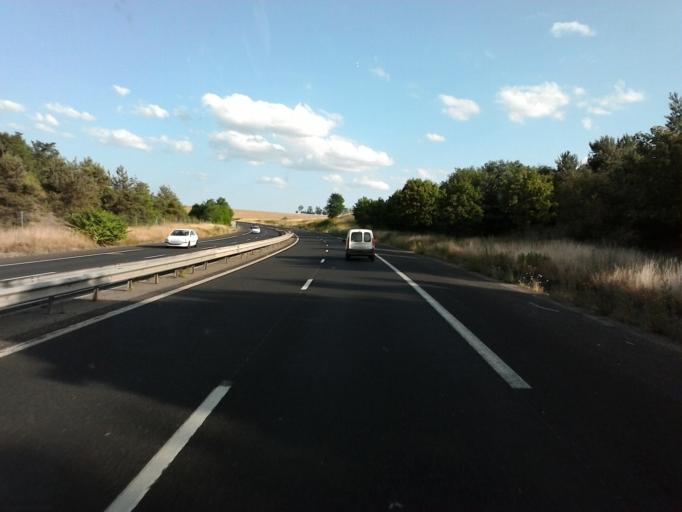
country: FR
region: Lorraine
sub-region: Departement de Meurthe-et-Moselle
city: Flavigny-sur-Moselle
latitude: 48.5644
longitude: 6.1761
